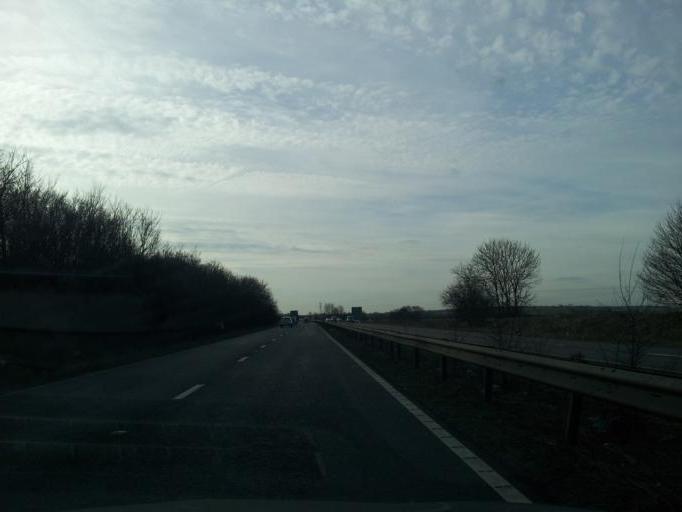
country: GB
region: England
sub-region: Cambridgeshire
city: Brampton
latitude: 52.3457
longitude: -0.2517
